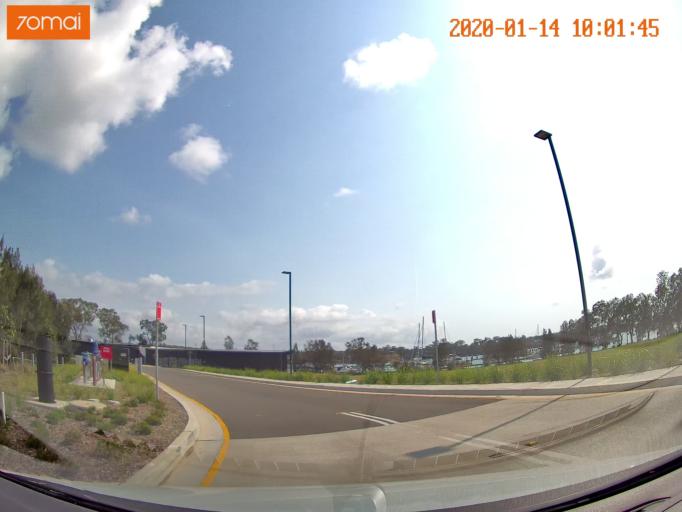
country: AU
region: New South Wales
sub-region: Wyong Shire
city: Kingfisher Shores
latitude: -33.1237
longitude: 151.5403
